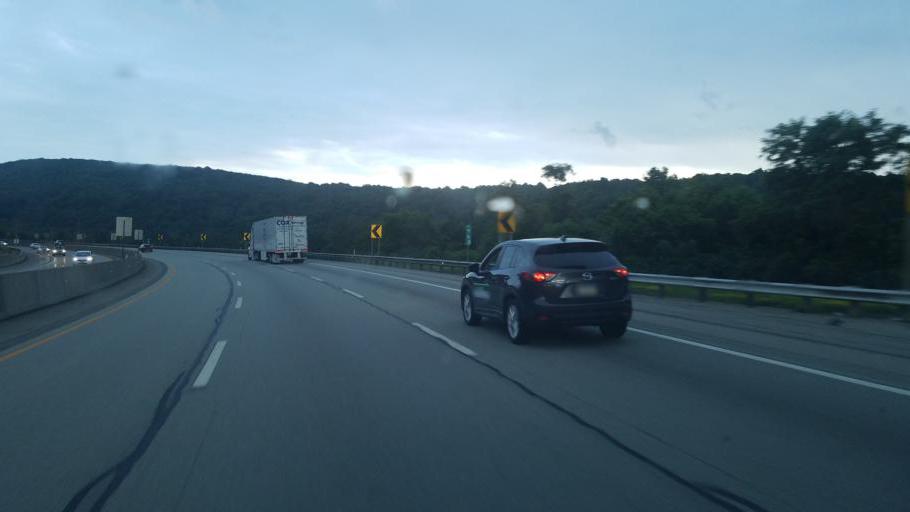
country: US
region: Pennsylvania
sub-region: Westmoreland County
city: Ligonier
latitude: 40.1201
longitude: -79.2787
